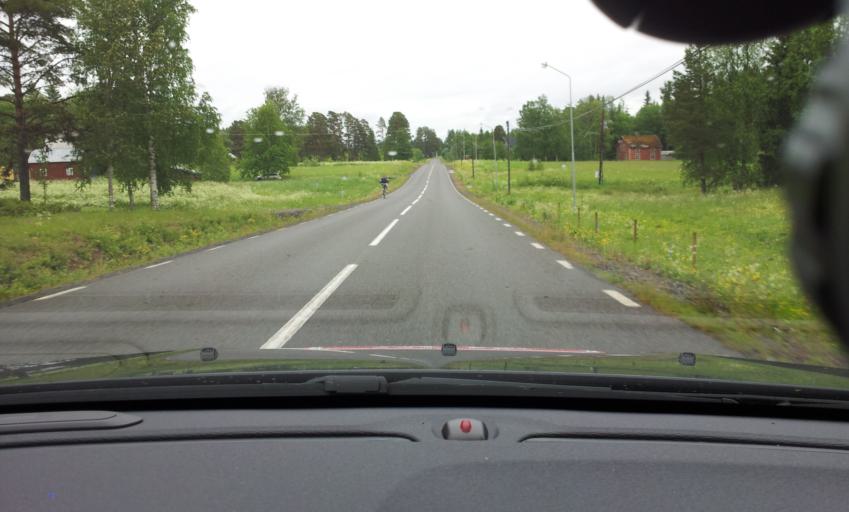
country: SE
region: Jaemtland
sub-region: OEstersunds Kommun
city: Lit
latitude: 63.7194
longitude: 14.9649
